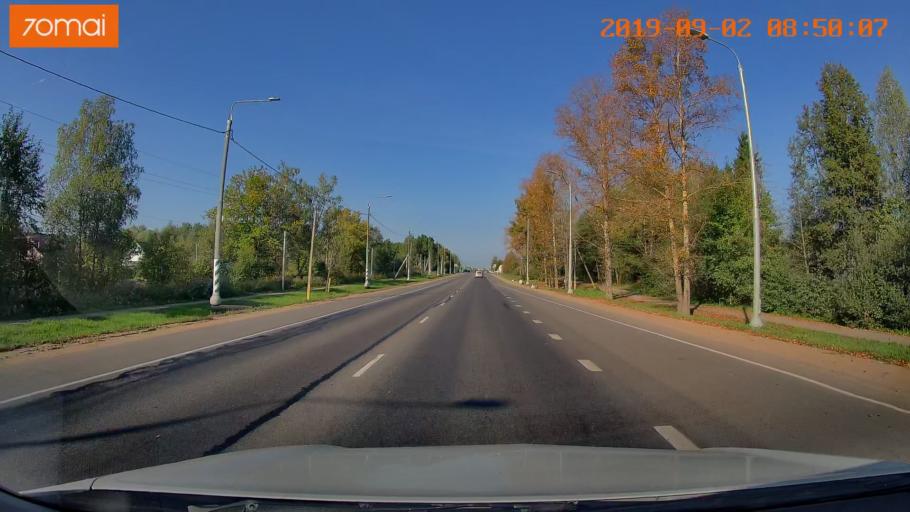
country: RU
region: Kaluga
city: Medyn'
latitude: 54.9656
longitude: 35.8919
